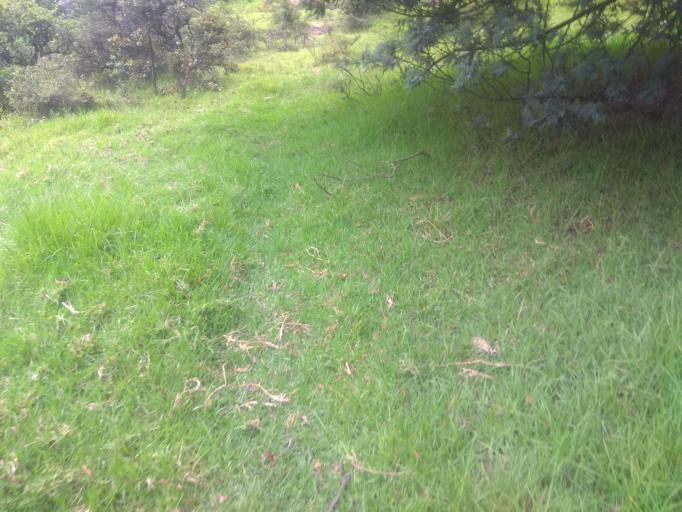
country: CO
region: Boyaca
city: Socota
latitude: 6.0181
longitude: -72.6593
